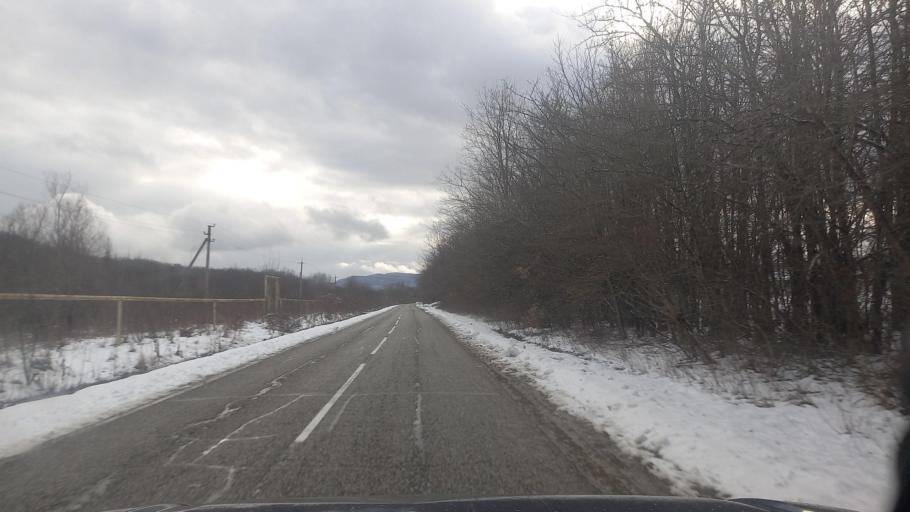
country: RU
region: Krasnodarskiy
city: Smolenskaya
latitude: 44.7471
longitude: 38.8400
